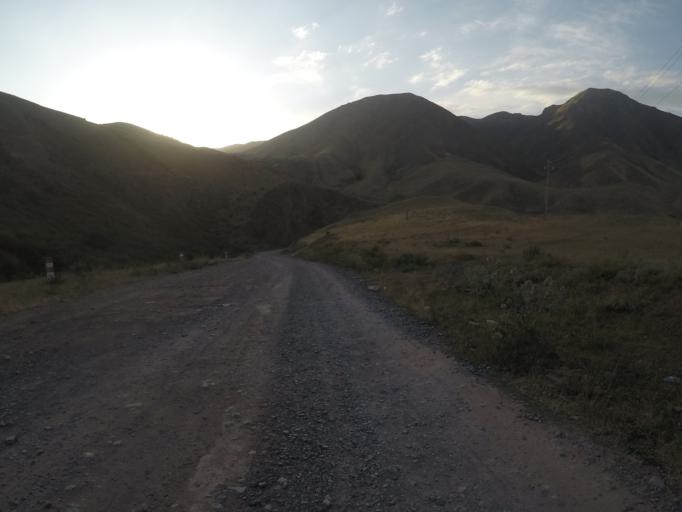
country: KG
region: Chuy
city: Bishkek
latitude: 42.6690
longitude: 74.6470
